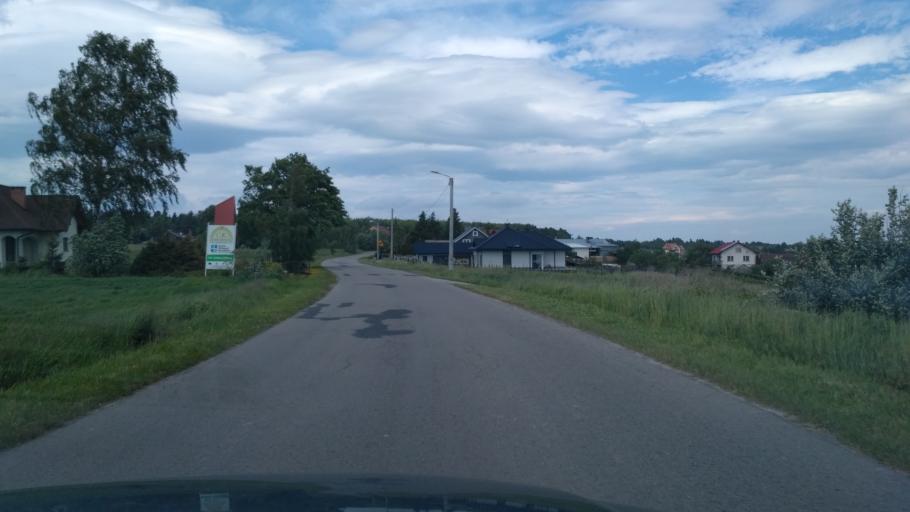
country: PL
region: Subcarpathian Voivodeship
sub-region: Powiat ropczycko-sedziszowski
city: Ropczyce
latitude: 49.9991
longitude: 21.6135
